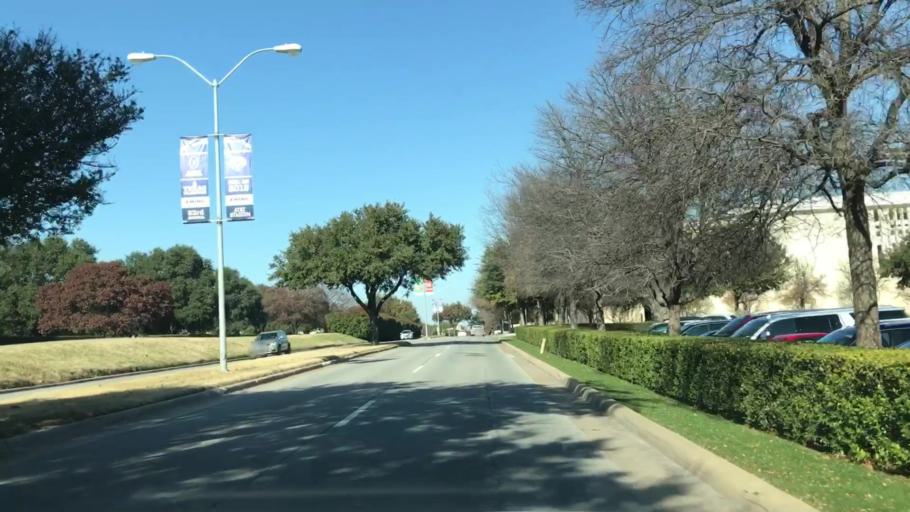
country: US
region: Texas
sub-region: Dallas County
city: University Park
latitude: 32.8681
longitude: -96.7764
